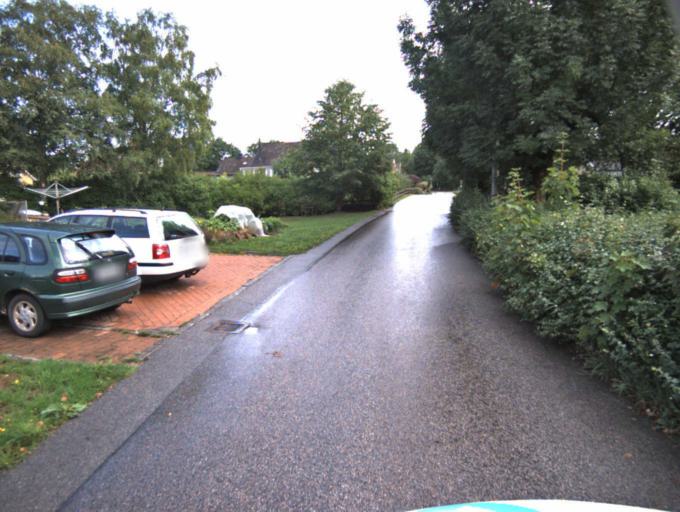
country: SE
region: Vaestra Goetaland
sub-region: Ulricehamns Kommun
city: Ulricehamn
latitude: 57.7207
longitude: 13.3049
